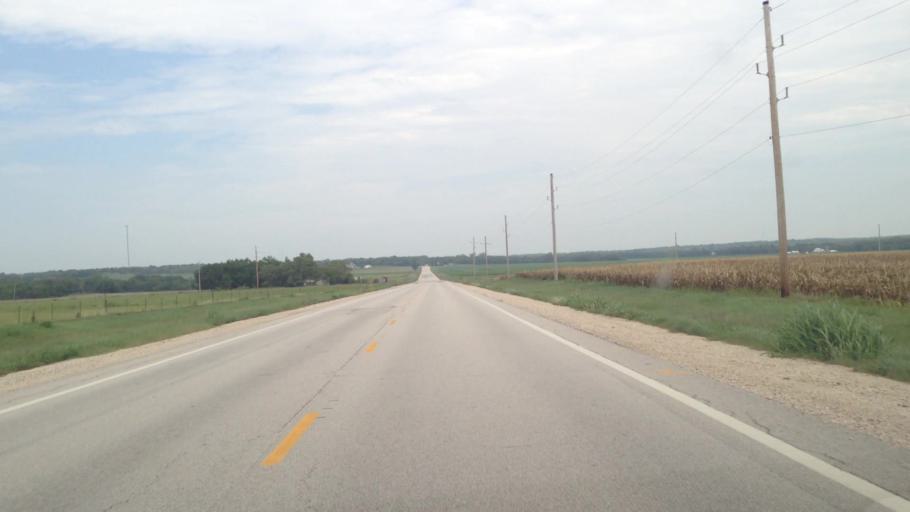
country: US
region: Kansas
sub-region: Anderson County
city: Garnett
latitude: 38.0635
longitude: -95.1693
